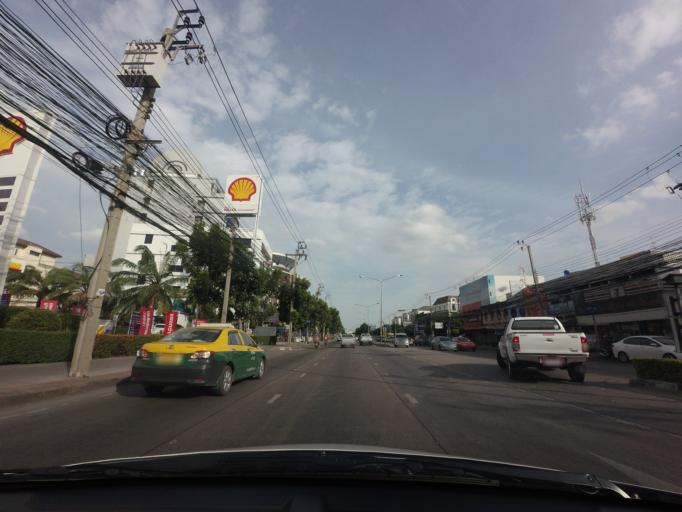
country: TH
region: Bangkok
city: Bueng Kum
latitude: 13.7998
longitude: 100.6493
